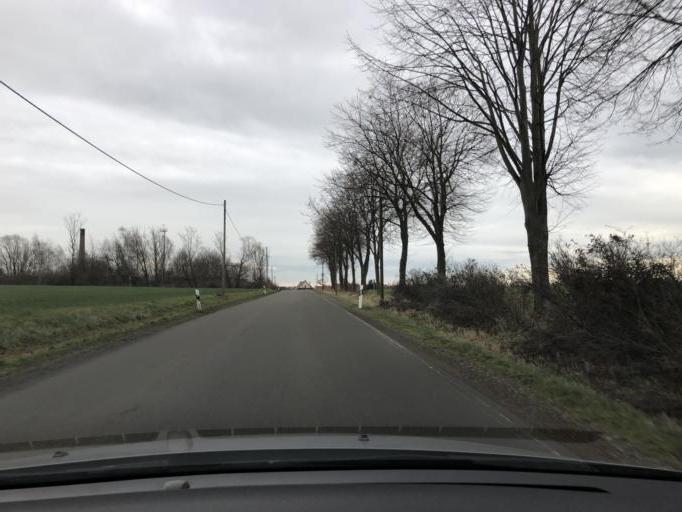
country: DE
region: Saxony
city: Nossen
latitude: 51.0792
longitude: 13.2840
